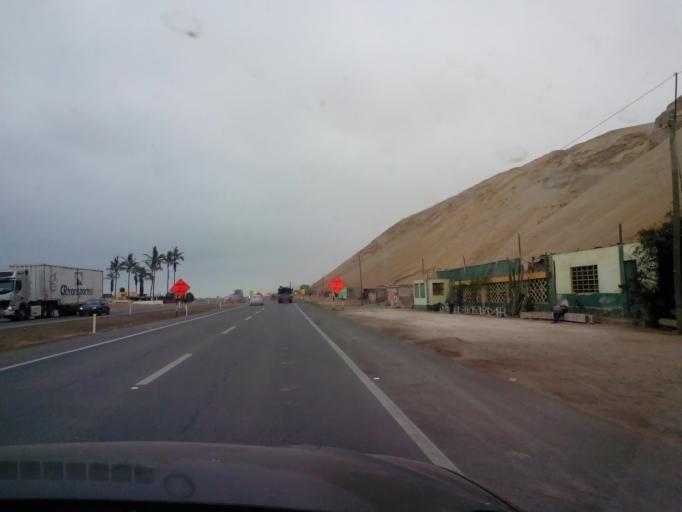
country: PE
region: Ica
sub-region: Provincia de Chincha
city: San Pedro
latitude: -13.3299
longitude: -76.2386
